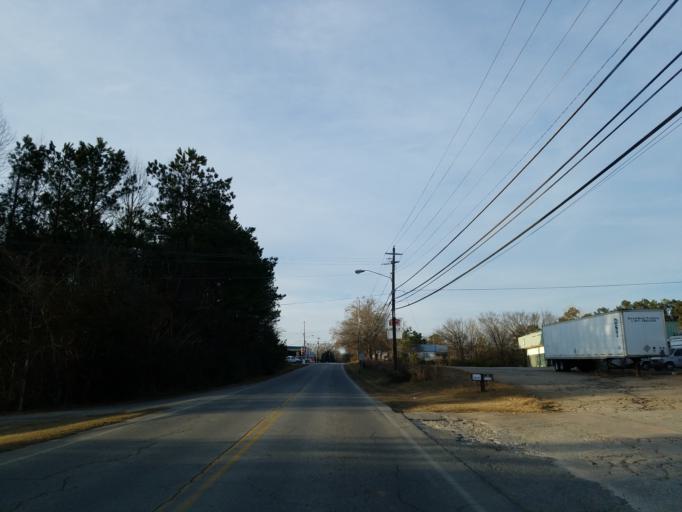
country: US
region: Georgia
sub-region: Cobb County
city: Acworth
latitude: 34.0756
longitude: -84.6908
